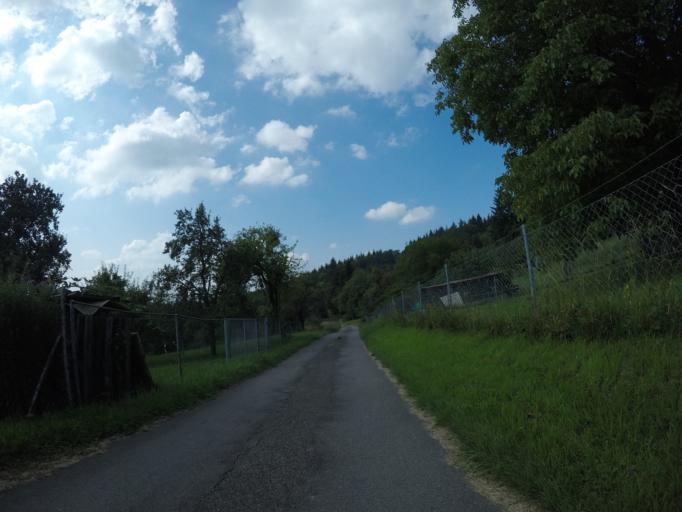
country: DE
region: Baden-Wuerttemberg
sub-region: Tuebingen Region
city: Pfullingen
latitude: 48.4626
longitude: 9.1994
